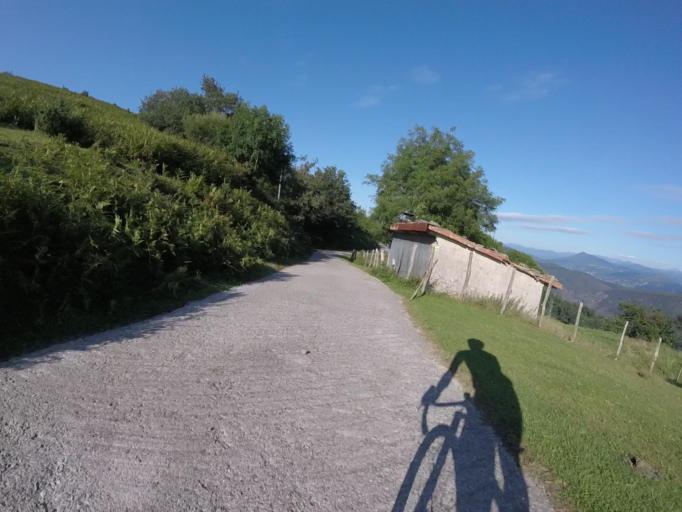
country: ES
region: Basque Country
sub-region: Provincia de Guipuzcoa
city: Irun
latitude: 43.2987
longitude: -1.7509
